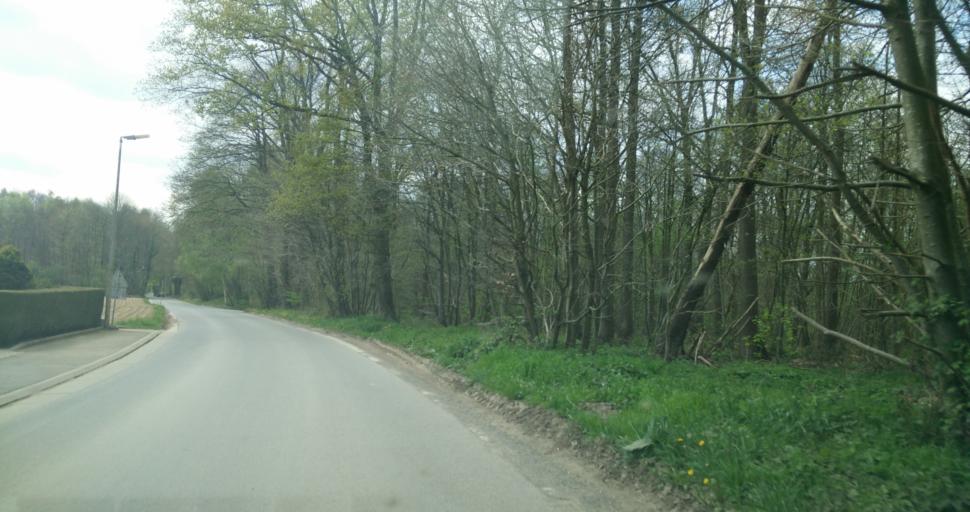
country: BE
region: Wallonia
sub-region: Province du Hainaut
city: Braine-le-Comte
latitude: 50.6347
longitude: 4.1964
